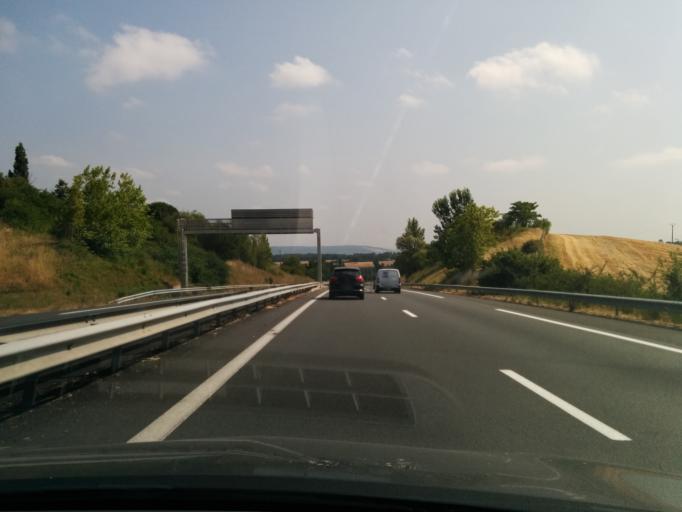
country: FR
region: Midi-Pyrenees
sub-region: Departement de la Haute-Garonne
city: Montastruc-la-Conseillere
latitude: 43.7325
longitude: 1.5782
